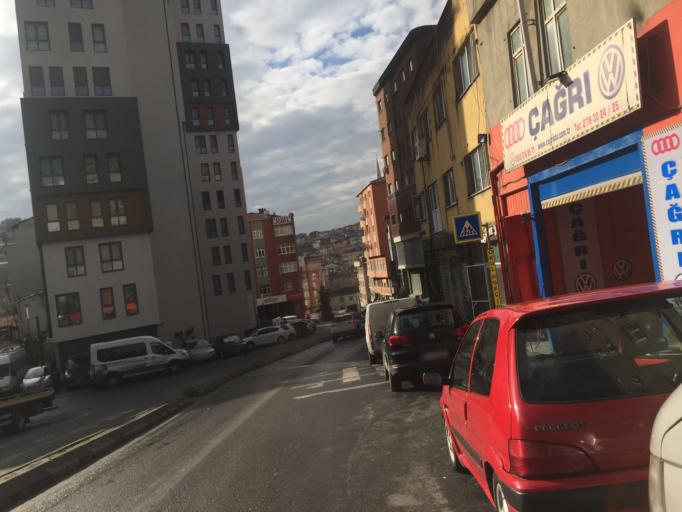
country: TR
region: Istanbul
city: Sisli
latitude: 41.0990
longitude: 28.9980
